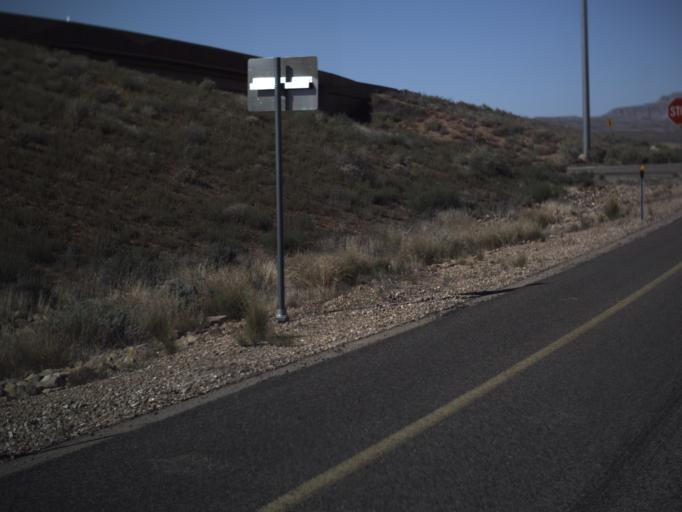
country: US
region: Utah
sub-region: Washington County
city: Saint George
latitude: 37.0011
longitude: -113.5594
